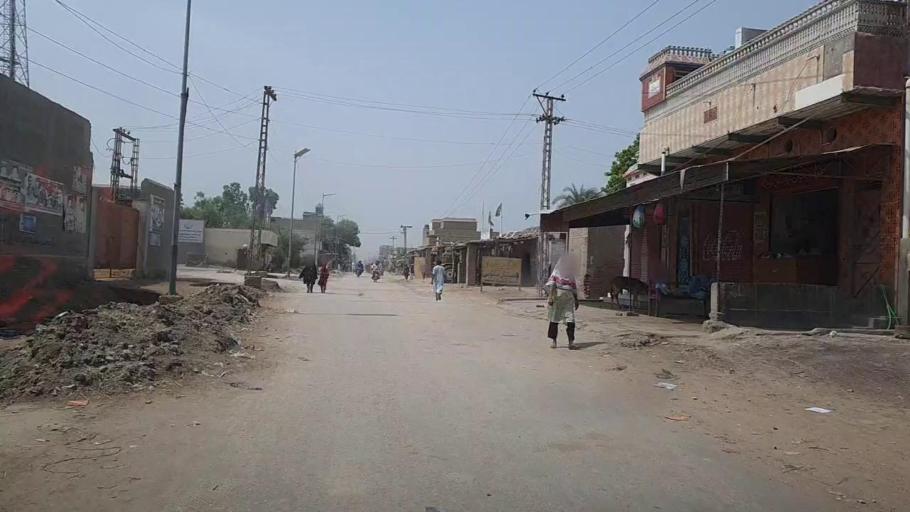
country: PK
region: Sindh
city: Radhan
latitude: 27.1756
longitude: 67.9487
